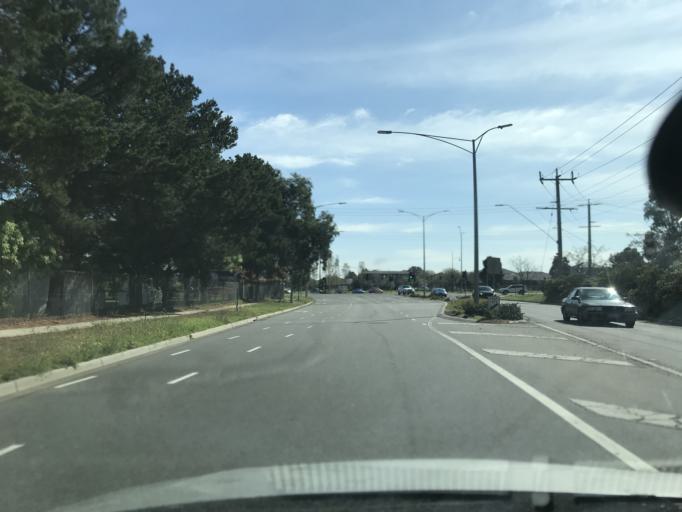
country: AU
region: Victoria
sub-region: Whittlesea
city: Epping
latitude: -37.6380
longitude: 145.0216
